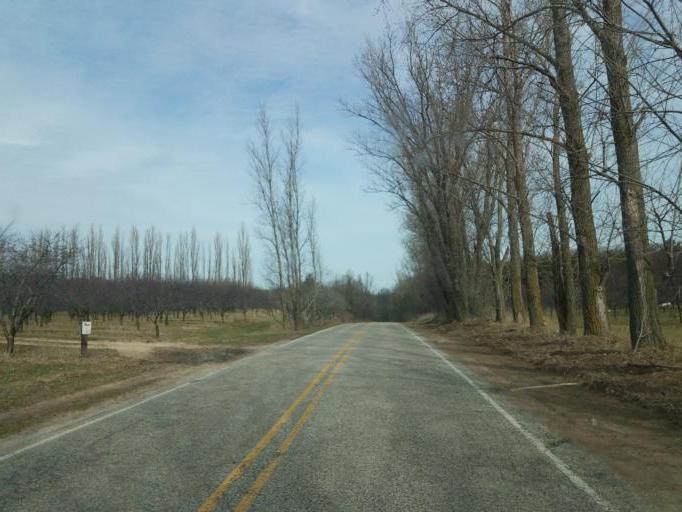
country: US
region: Michigan
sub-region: Oceana County
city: Shelby
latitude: 43.6401
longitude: -86.5123
